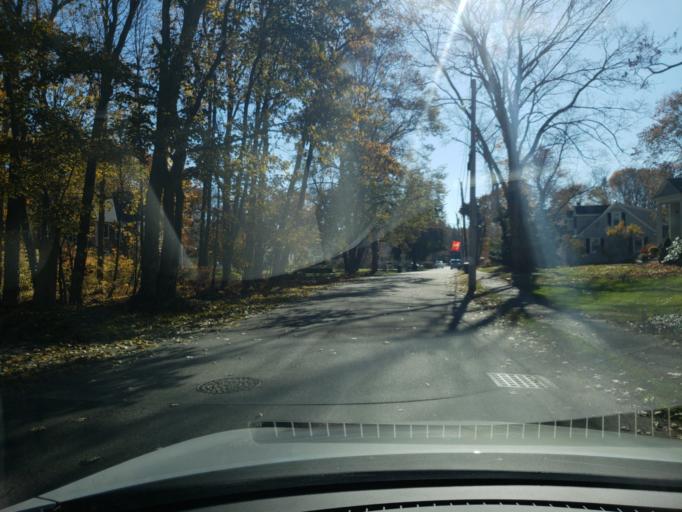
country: US
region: Massachusetts
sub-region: Essex County
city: Andover
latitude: 42.6608
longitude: -71.1306
